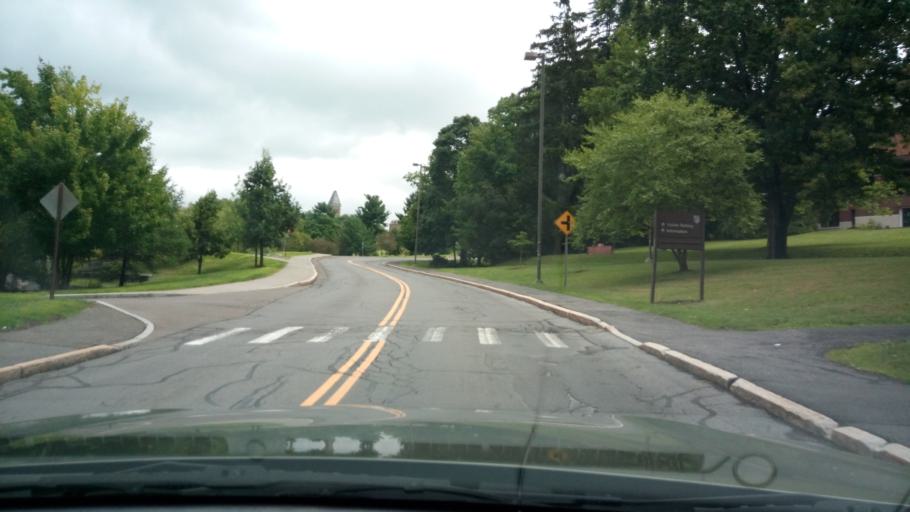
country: US
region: New York
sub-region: Tompkins County
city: Ithaca
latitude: 42.4456
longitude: -76.4880
